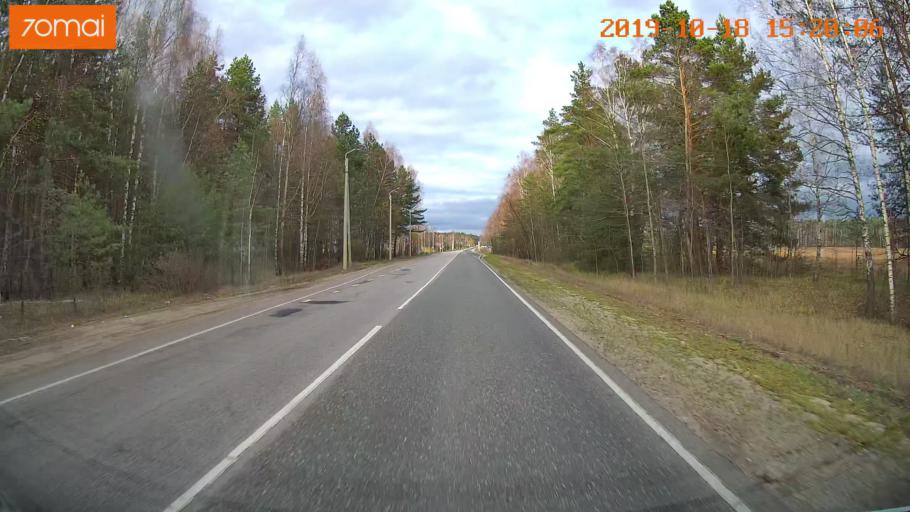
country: RU
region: Vladimir
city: Anopino
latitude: 55.6828
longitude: 40.7426
